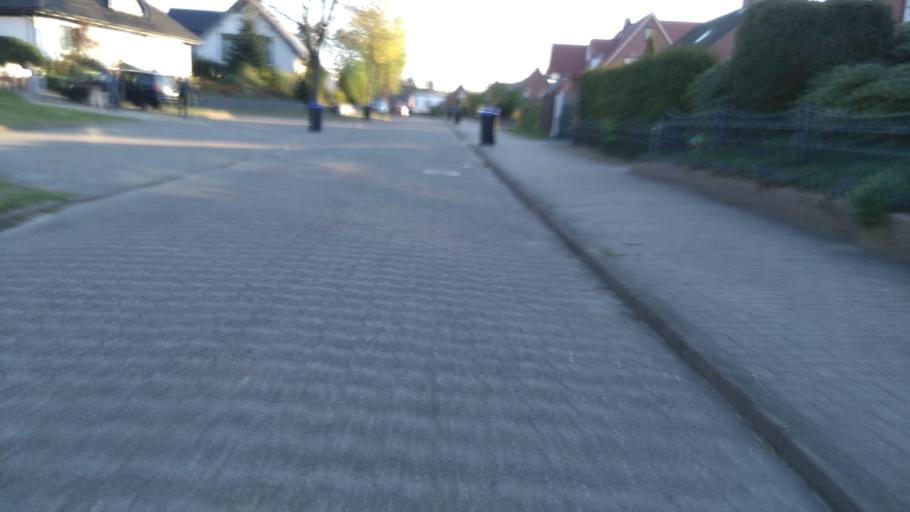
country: DE
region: Lower Saxony
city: Harsefeld
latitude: 53.4682
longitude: 9.5087
